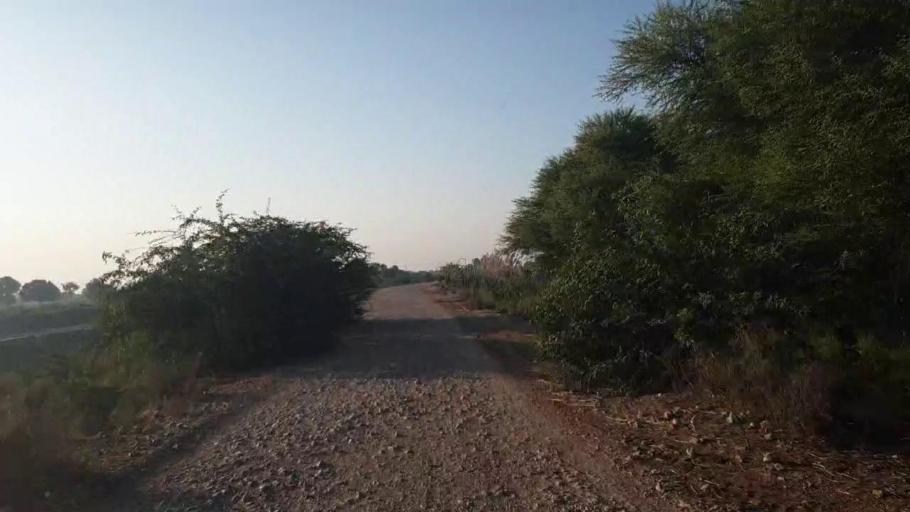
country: PK
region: Sindh
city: Badin
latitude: 24.6538
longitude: 68.7896
